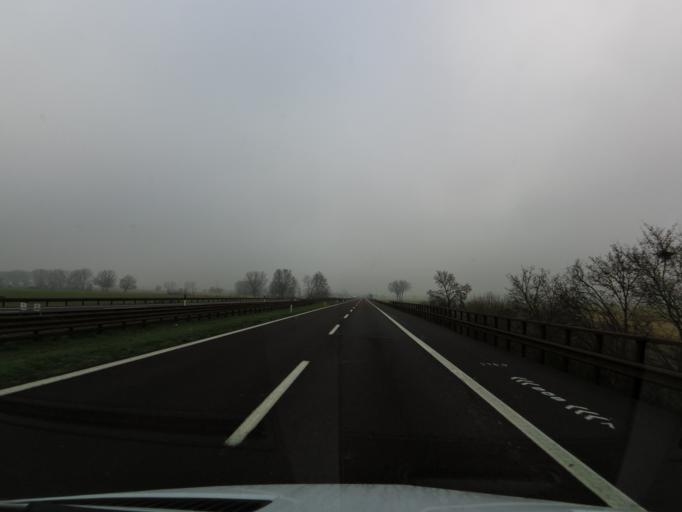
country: IT
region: Lombardy
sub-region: Provincia di Mantova
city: Pegognaga
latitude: 44.9705
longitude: 10.8576
